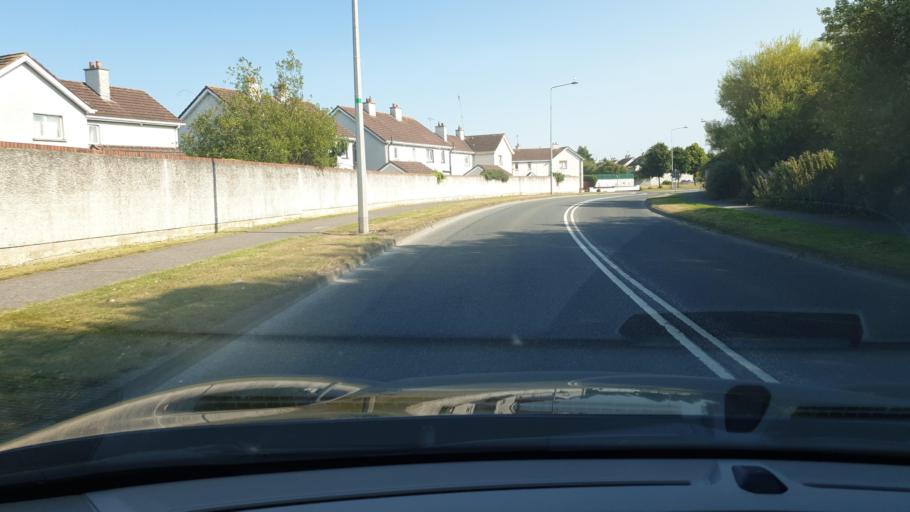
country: IE
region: Leinster
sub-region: An Mhi
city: Navan
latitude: 53.6497
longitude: -6.7025
